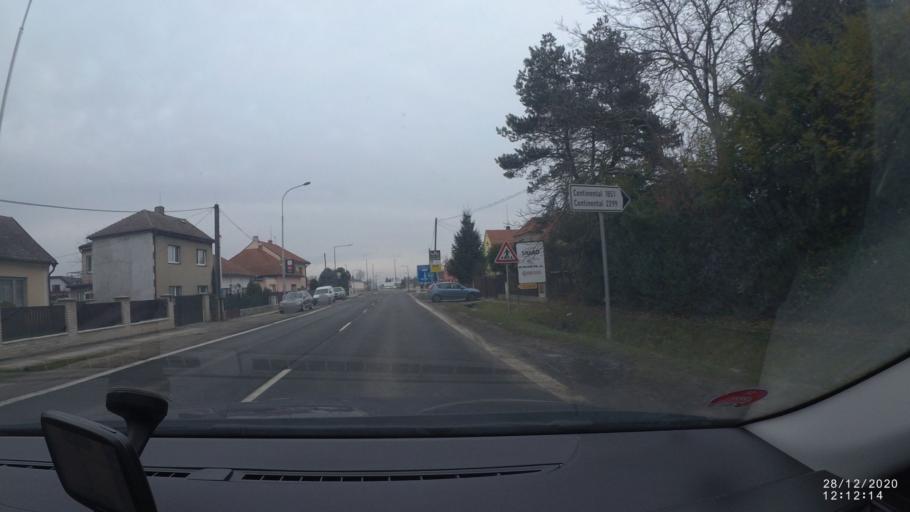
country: CZ
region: Central Bohemia
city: Brandys nad Labem-Stara Boleslav
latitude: 50.1766
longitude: 14.6521
